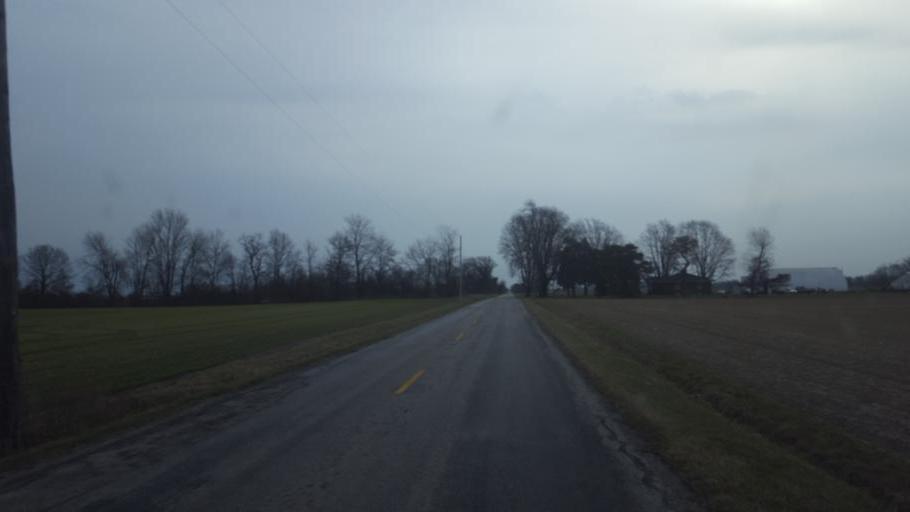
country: US
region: Ohio
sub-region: Marion County
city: Marion
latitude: 40.6522
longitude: -83.0120
